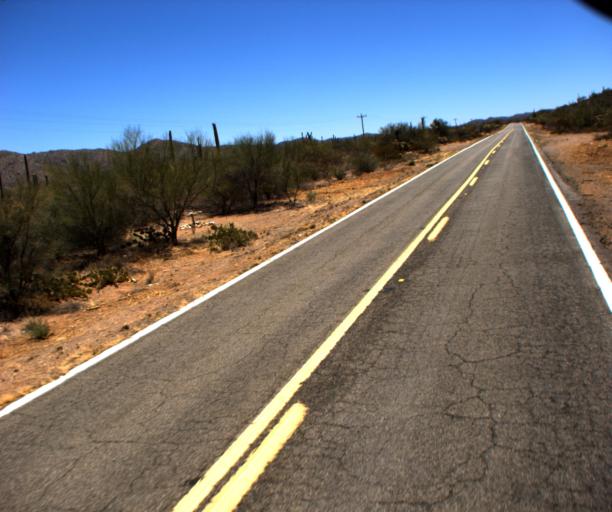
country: US
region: Arizona
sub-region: Pima County
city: Sells
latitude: 32.1778
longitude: -112.2713
